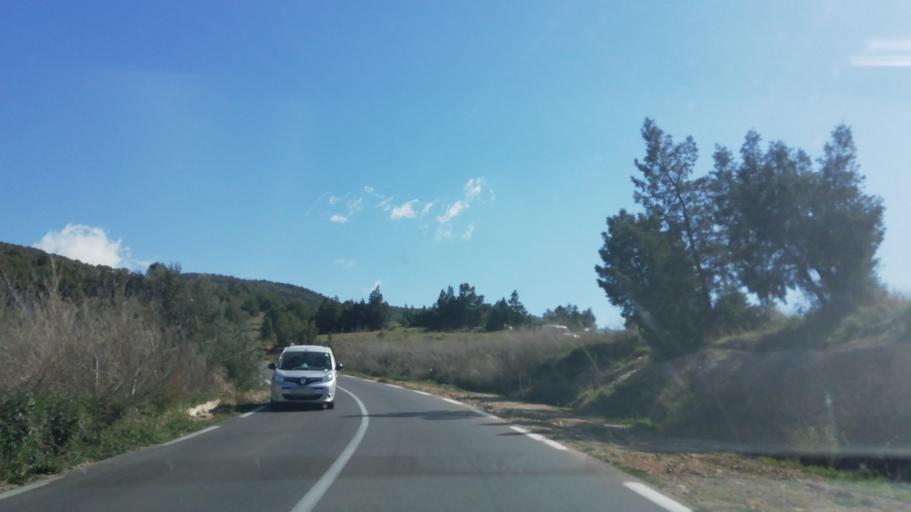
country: DZ
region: Mascara
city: Mascara
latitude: 35.4887
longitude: 0.1410
